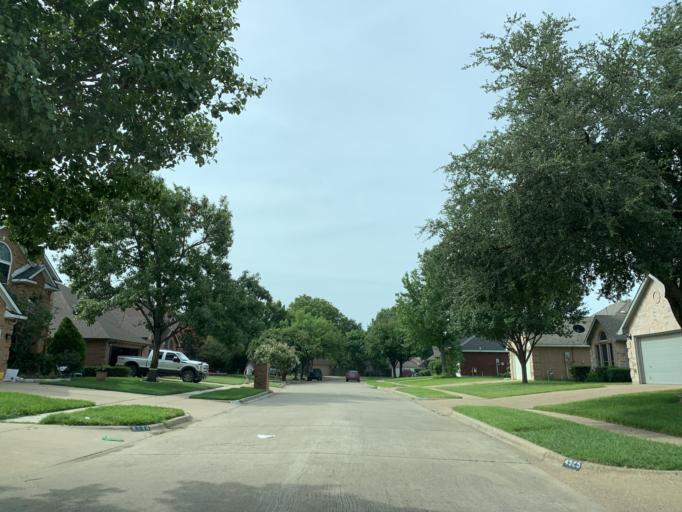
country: US
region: Texas
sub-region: Dallas County
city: Grand Prairie
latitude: 32.6597
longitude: -97.0073
